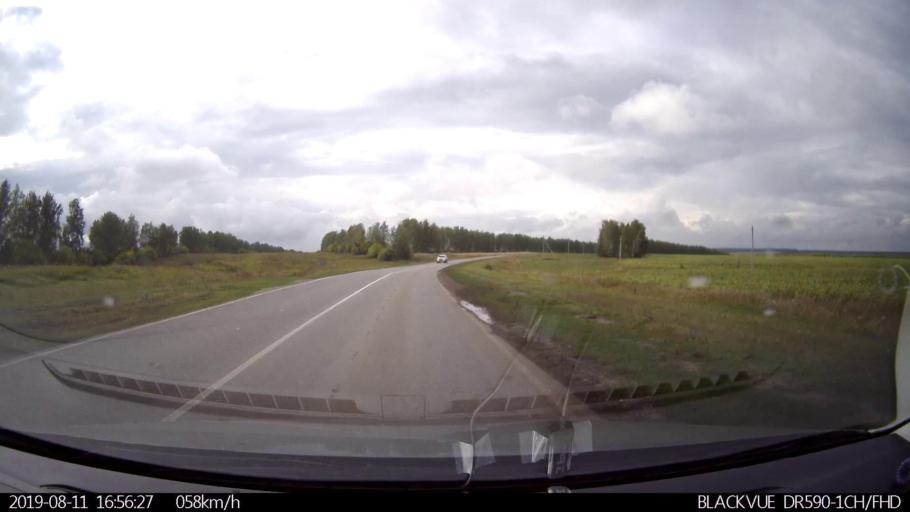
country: RU
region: Ulyanovsk
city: Mayna
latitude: 54.2877
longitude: 47.6536
